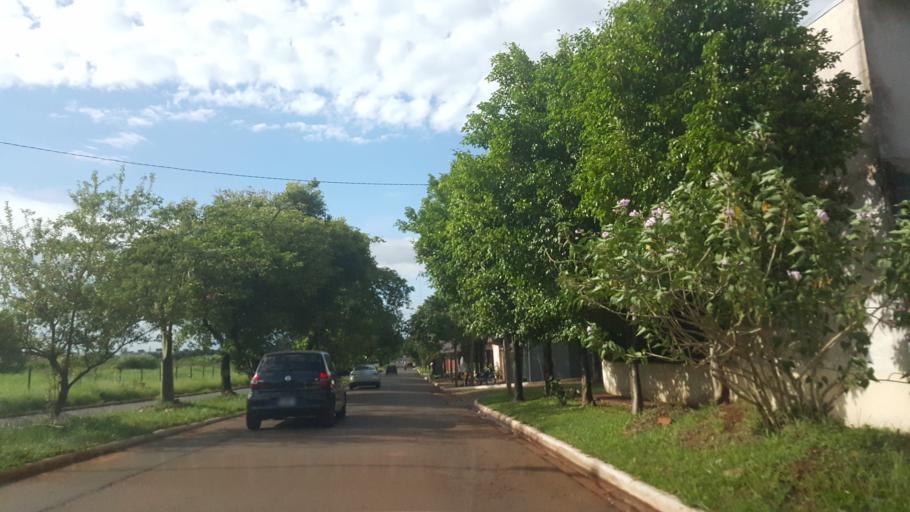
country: AR
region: Misiones
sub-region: Departamento de Capital
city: Posadas
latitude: -27.3771
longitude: -55.9330
